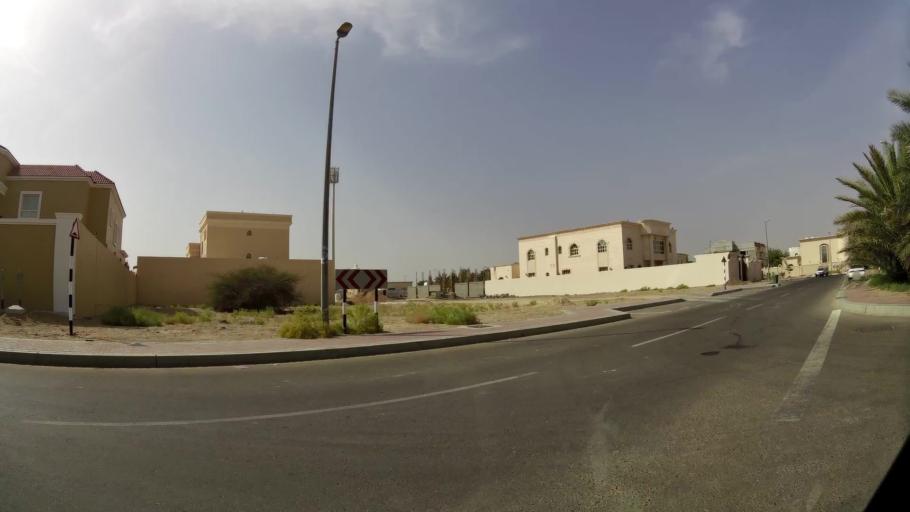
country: AE
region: Abu Dhabi
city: Al Ain
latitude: 24.1524
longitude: 55.7060
